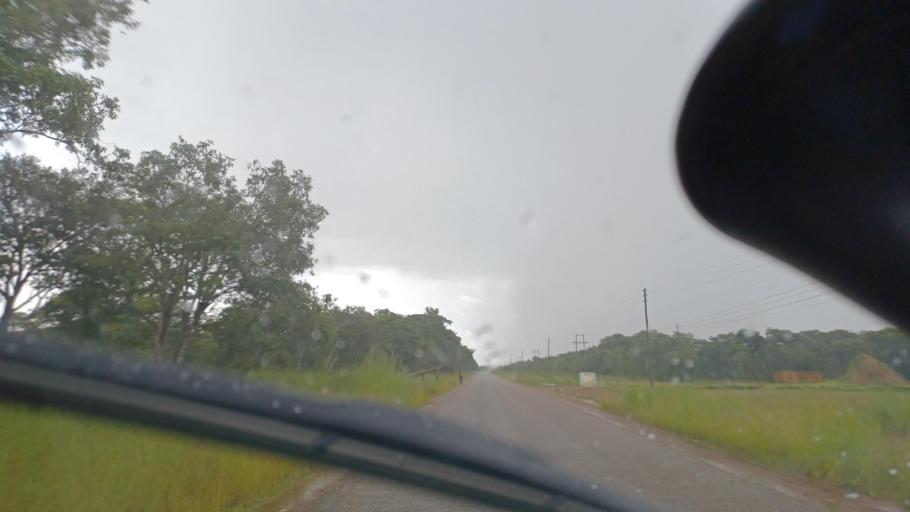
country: ZM
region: North-Western
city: Kasempa
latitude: -13.0912
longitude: 25.9367
